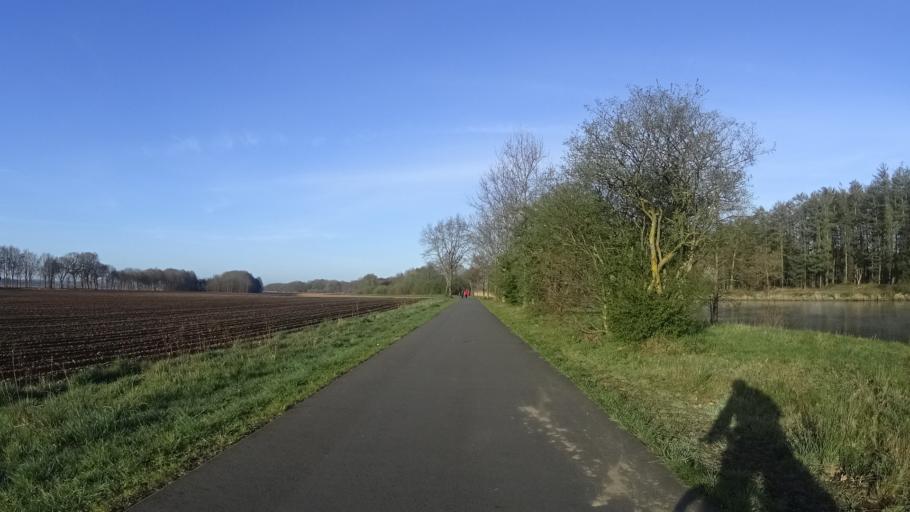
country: DE
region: Lower Saxony
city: Niederlangen
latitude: 52.8481
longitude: 7.3010
